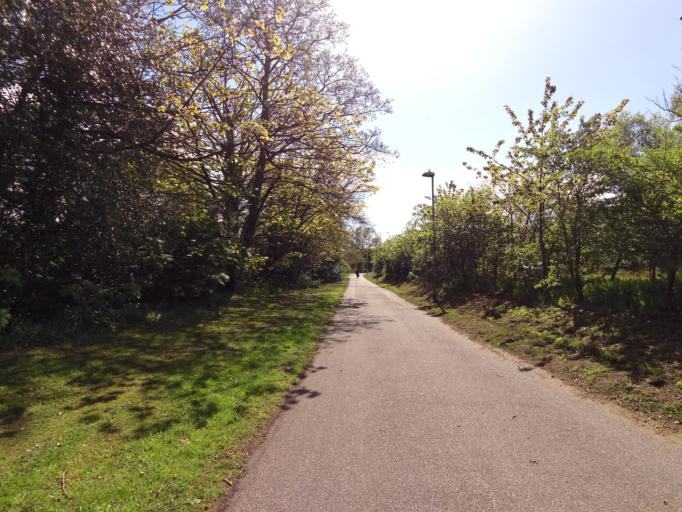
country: GB
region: England
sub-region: Suffolk
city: Lowestoft
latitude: 52.4578
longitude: 1.7219
